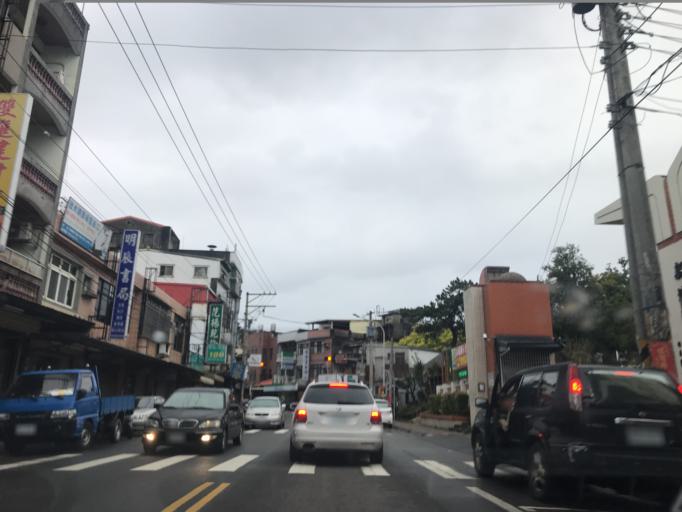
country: TW
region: Taiwan
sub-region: Hsinchu
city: Zhubei
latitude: 24.8279
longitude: 121.0797
